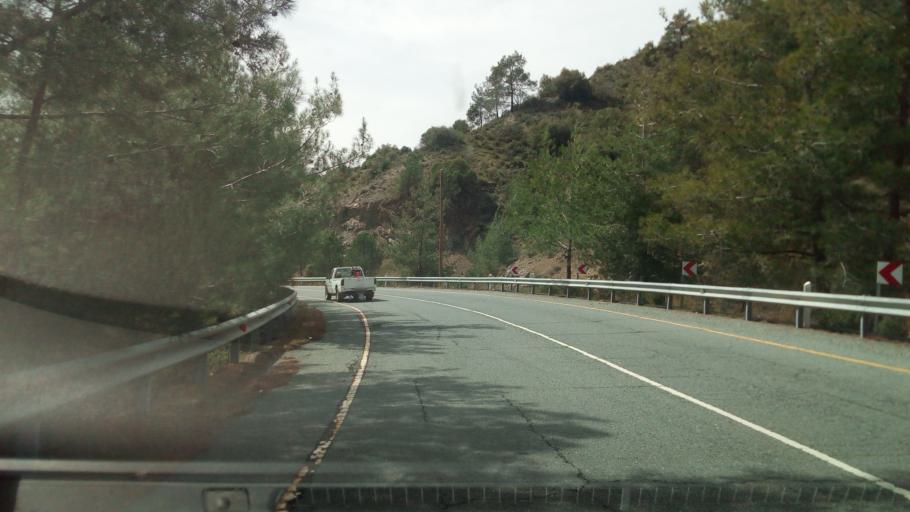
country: CY
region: Limassol
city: Pelendri
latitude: 34.8661
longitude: 32.9226
